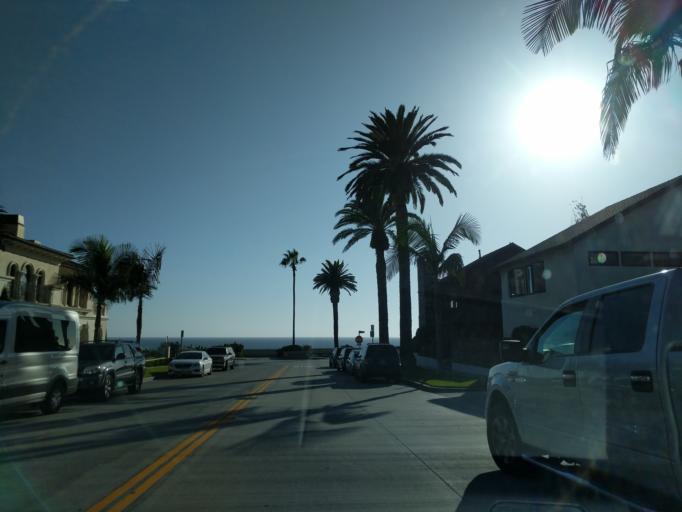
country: US
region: California
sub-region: Orange County
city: San Joaquin Hills
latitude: 33.5943
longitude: -117.8729
